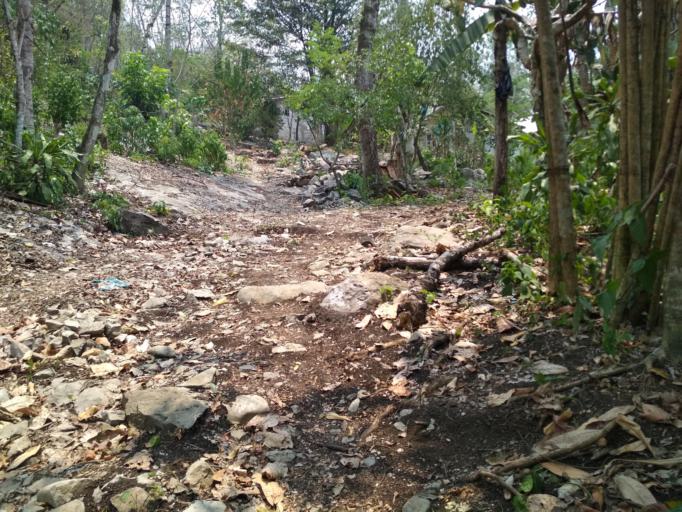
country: MX
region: Veracruz
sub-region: Tezonapa
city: Laguna Chica (Pueblo Nuevo)
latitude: 18.5372
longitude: -96.7275
